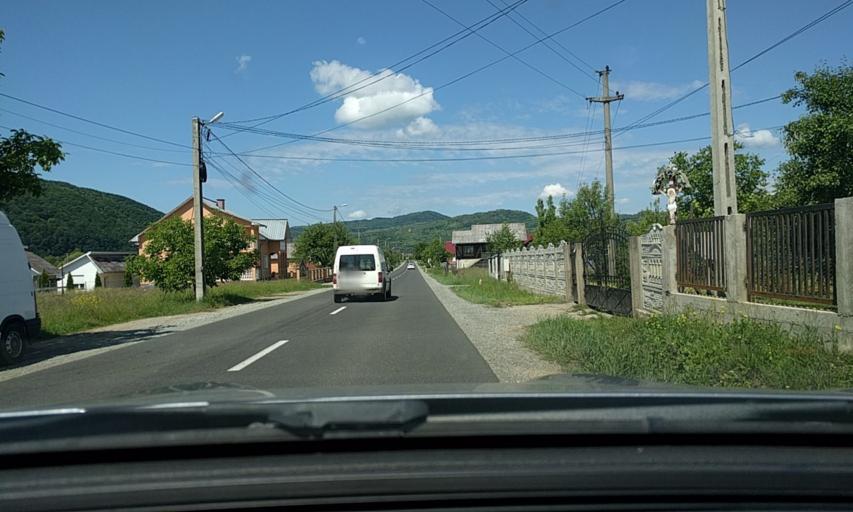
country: RO
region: Bistrita-Nasaud
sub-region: Comuna Salva
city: Salva
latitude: 47.2978
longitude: 24.3765
